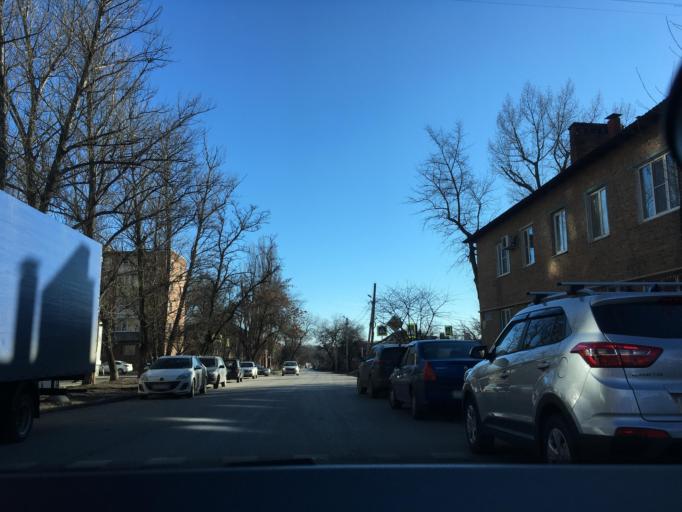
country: RU
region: Rostov
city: Imeni Chkalova
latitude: 47.2670
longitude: 39.7886
